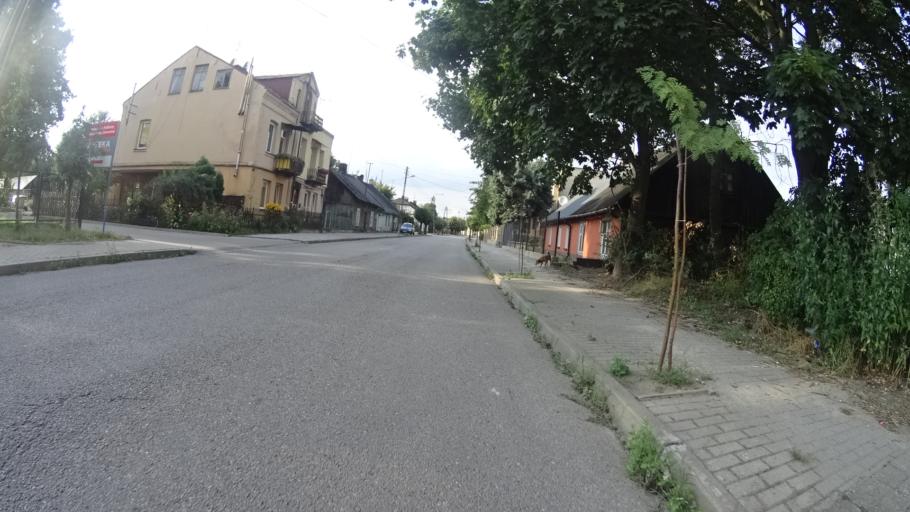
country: PL
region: Masovian Voivodeship
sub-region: Powiat grojecki
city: Mogielnica
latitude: 51.6905
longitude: 20.7260
